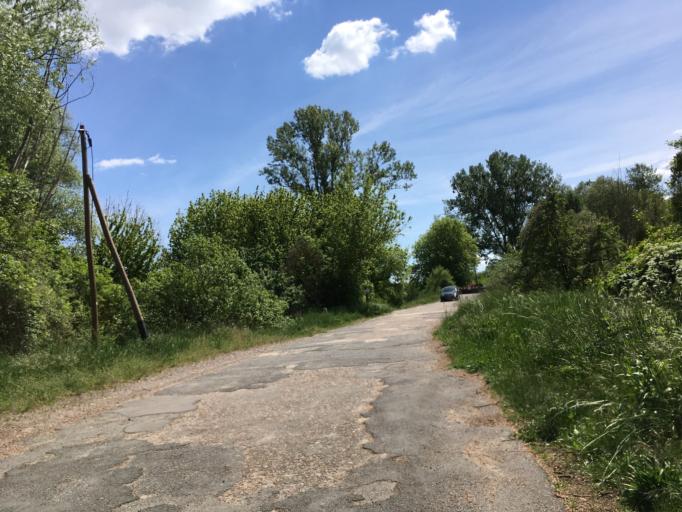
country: DE
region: Brandenburg
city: Liepe
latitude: 52.8597
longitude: 13.9707
